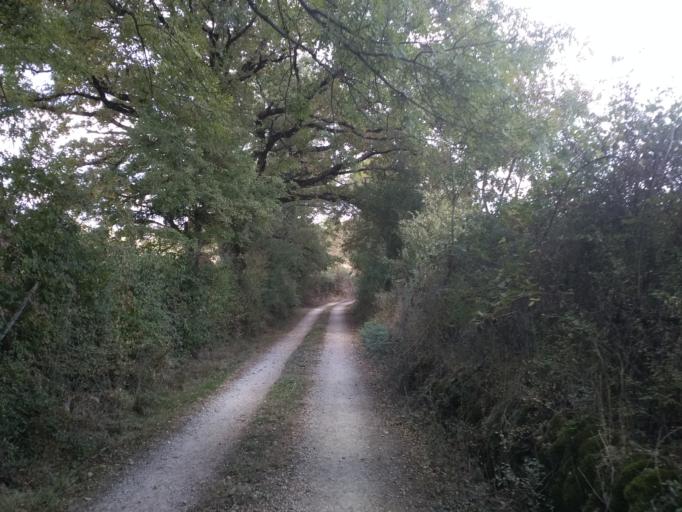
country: FR
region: Midi-Pyrenees
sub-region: Departement de l'Aveyron
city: Bozouls
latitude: 44.4704
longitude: 2.6769
